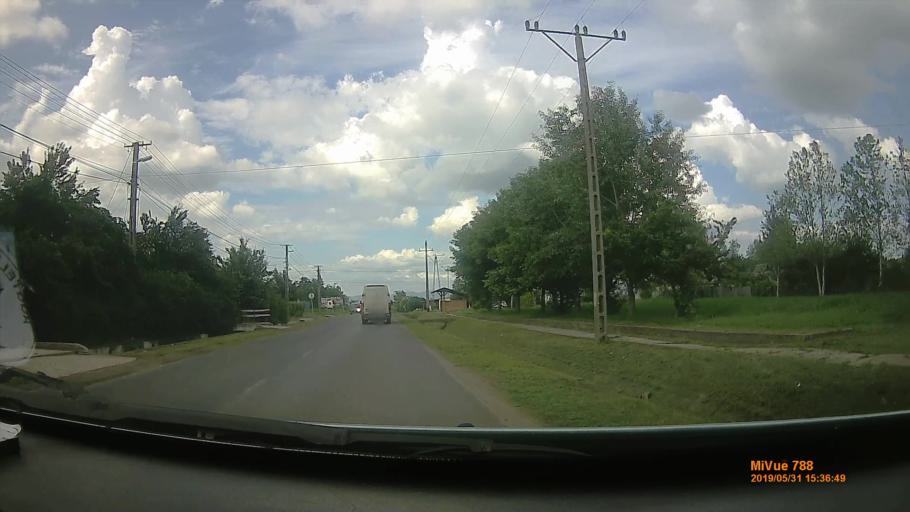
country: HU
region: Borsod-Abauj-Zemplen
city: Prugy
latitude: 48.0869
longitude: 21.2406
